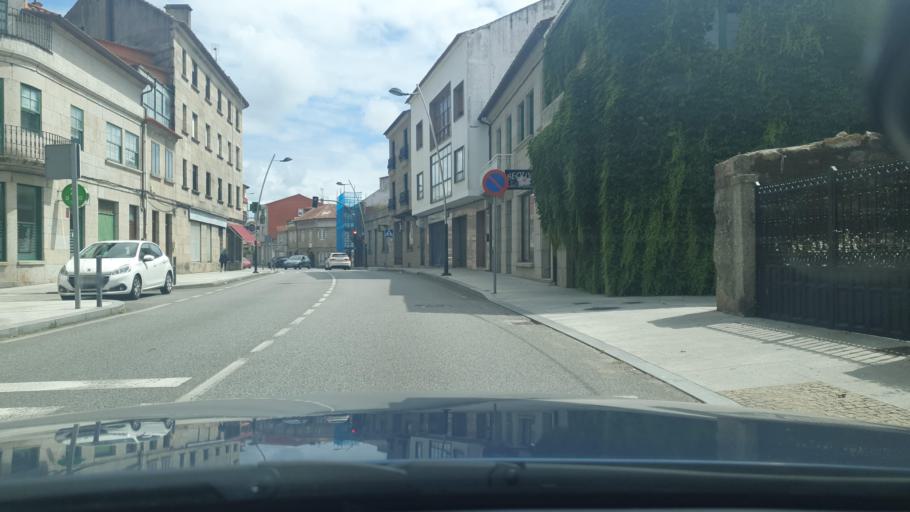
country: ES
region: Galicia
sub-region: Provincia de Pontevedra
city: Cambados
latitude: 42.5116
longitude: -8.8159
